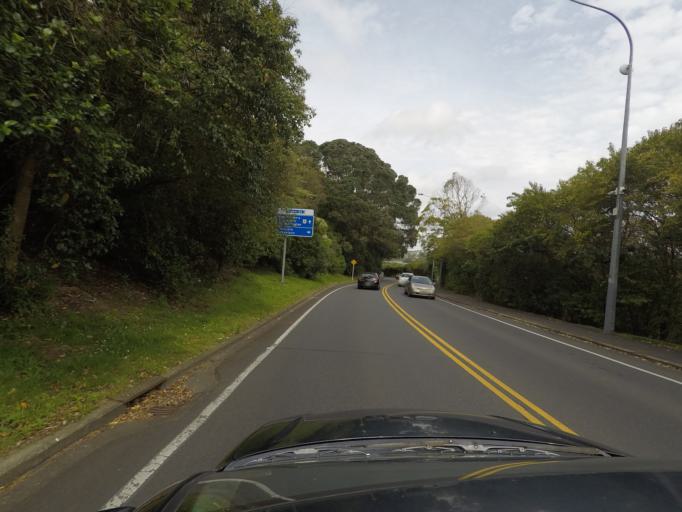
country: NZ
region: Auckland
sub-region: Auckland
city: Auckland
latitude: -36.8592
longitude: 174.8106
